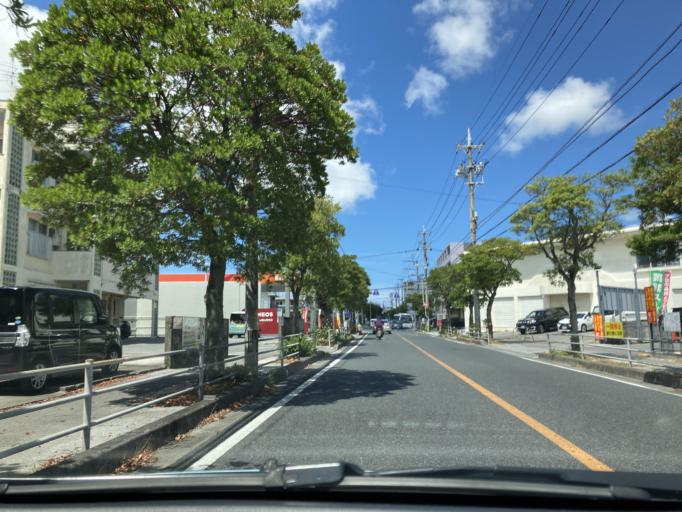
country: JP
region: Okinawa
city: Tomigusuku
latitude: 26.1830
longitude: 127.7138
